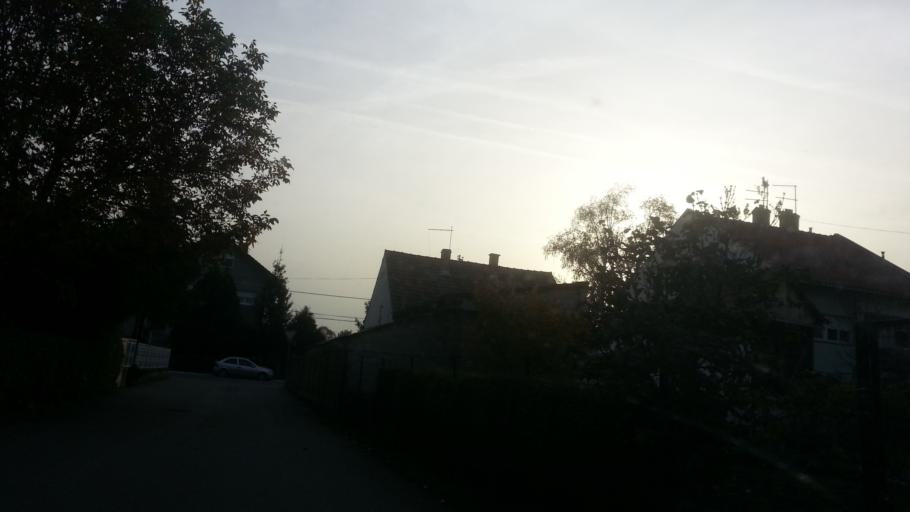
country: RS
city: Novi Banovci
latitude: 44.8974
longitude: 20.2854
